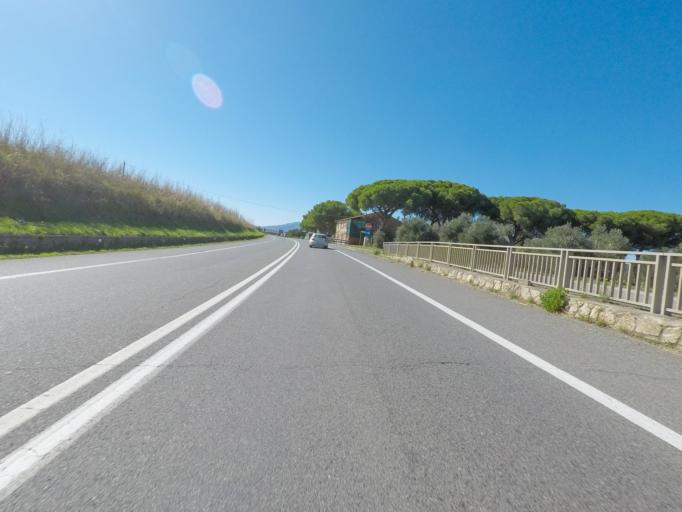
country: IT
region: Tuscany
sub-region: Provincia di Grosseto
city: Capalbio
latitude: 42.4152
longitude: 11.3407
